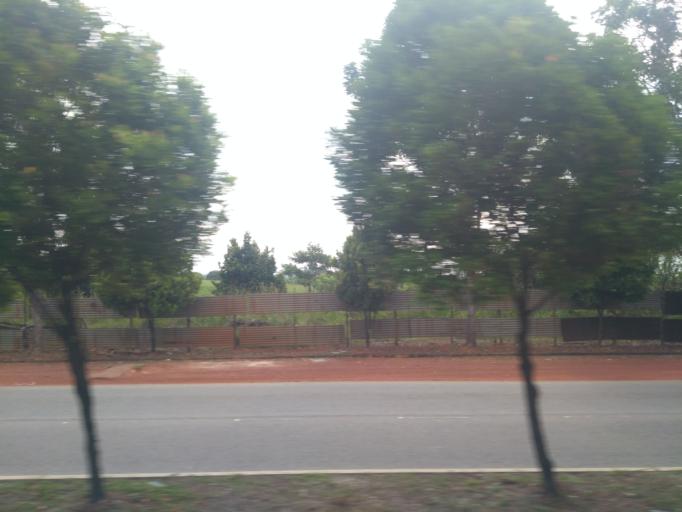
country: MY
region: Melaka
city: Kampung Ayer Keroh
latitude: 2.2753
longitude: 102.2598
